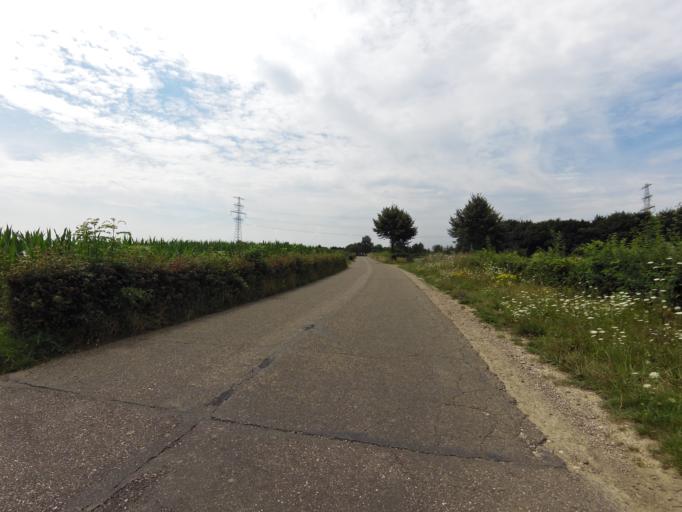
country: NL
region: Limburg
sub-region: Gemeente Voerendaal
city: Klimmen
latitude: 50.8711
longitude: 5.8710
